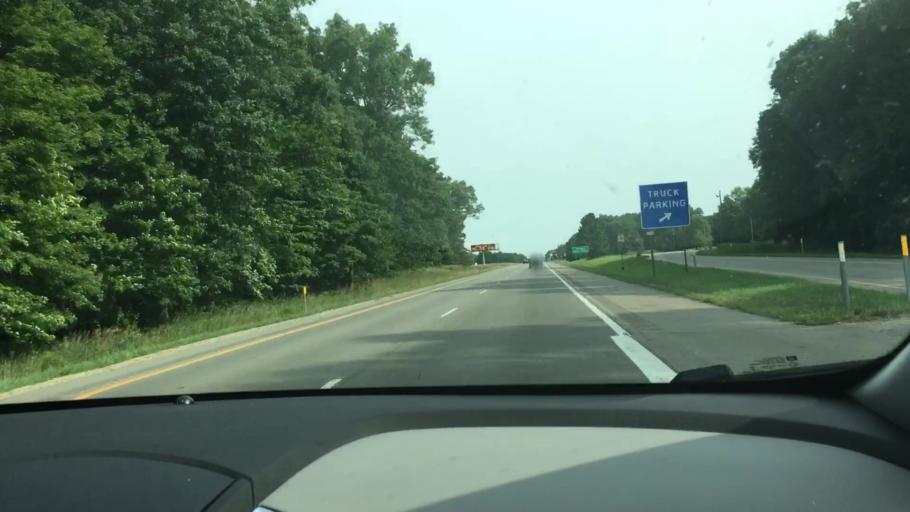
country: US
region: Michigan
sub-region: Kalamazoo County
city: Schoolcraft
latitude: 42.1699
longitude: -85.6447
